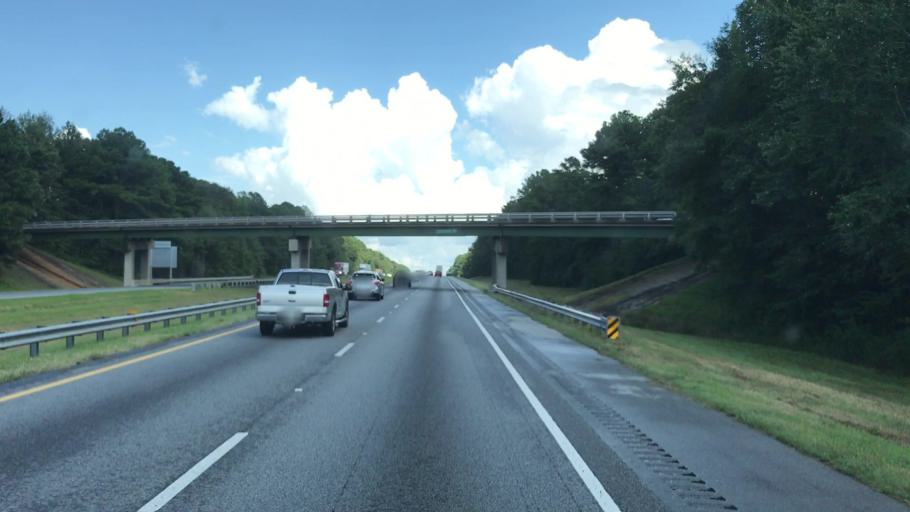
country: US
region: Georgia
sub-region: Walton County
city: Social Circle
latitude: 33.5871
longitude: -83.6114
